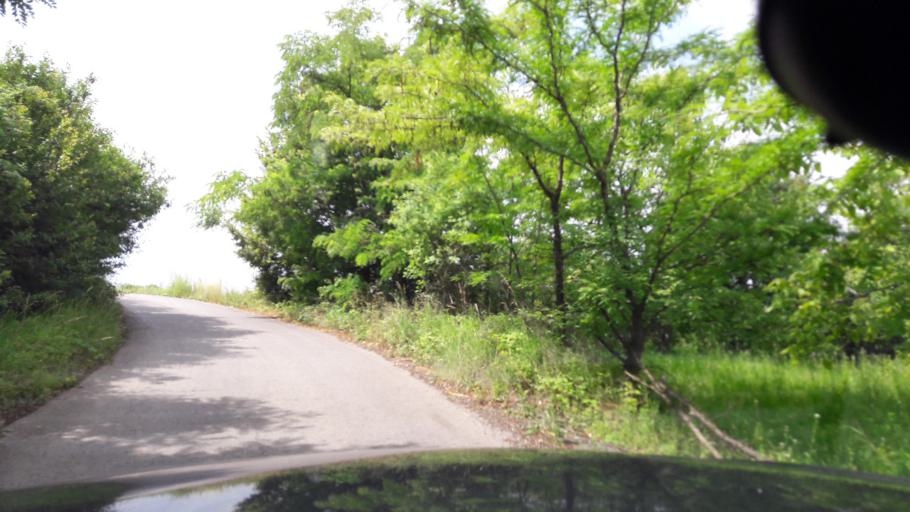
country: RS
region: Central Serbia
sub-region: Belgrade
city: Sopot
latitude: 44.6163
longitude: 20.5998
